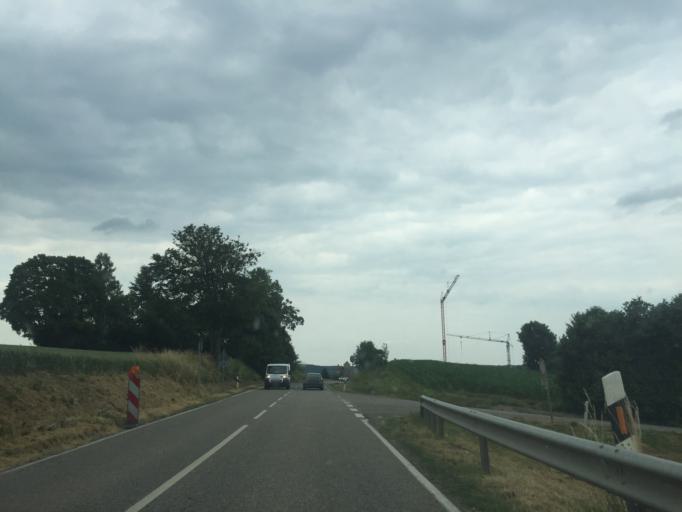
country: DE
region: Baden-Wuerttemberg
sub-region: Karlsruhe Region
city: Sinsheim
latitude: 49.2413
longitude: 8.8759
